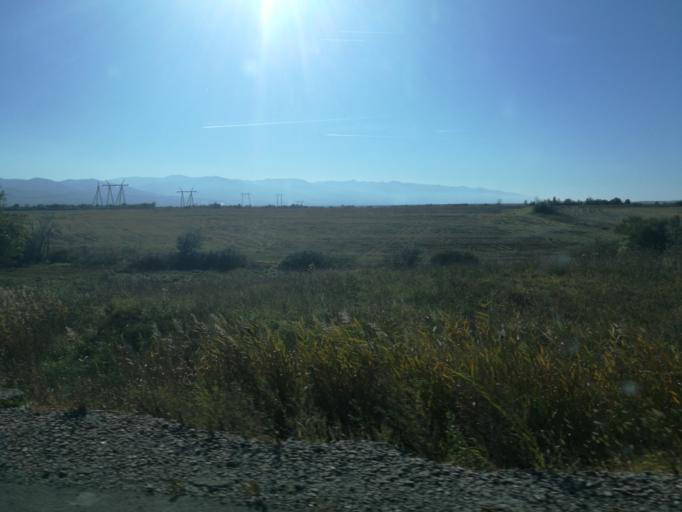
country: RO
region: Brasov
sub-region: Comuna Sinca Veche
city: Sinca Veche
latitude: 45.7995
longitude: 25.1788
